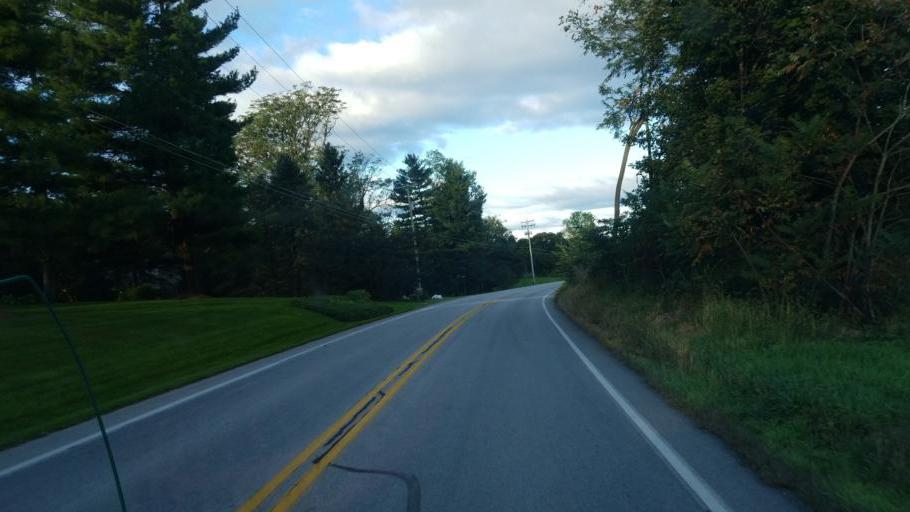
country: US
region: Pennsylvania
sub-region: Adams County
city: Lake Meade
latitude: 39.9358
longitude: -77.0494
